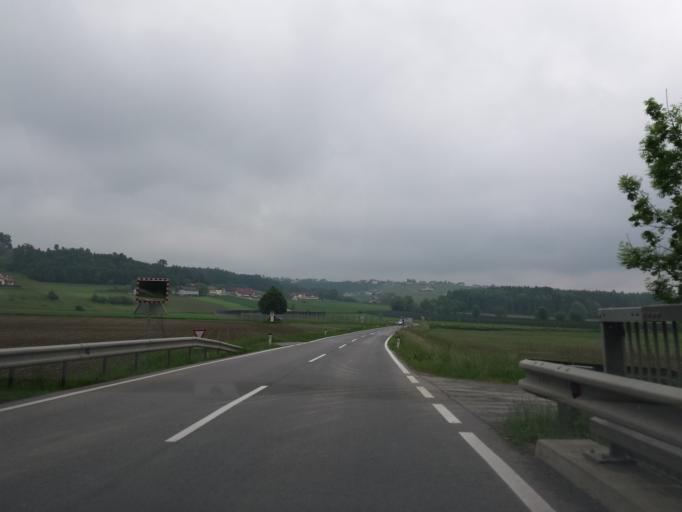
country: AT
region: Styria
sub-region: Politischer Bezirk Weiz
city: Mitterdorf an der Raab
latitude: 47.1715
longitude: 15.6174
